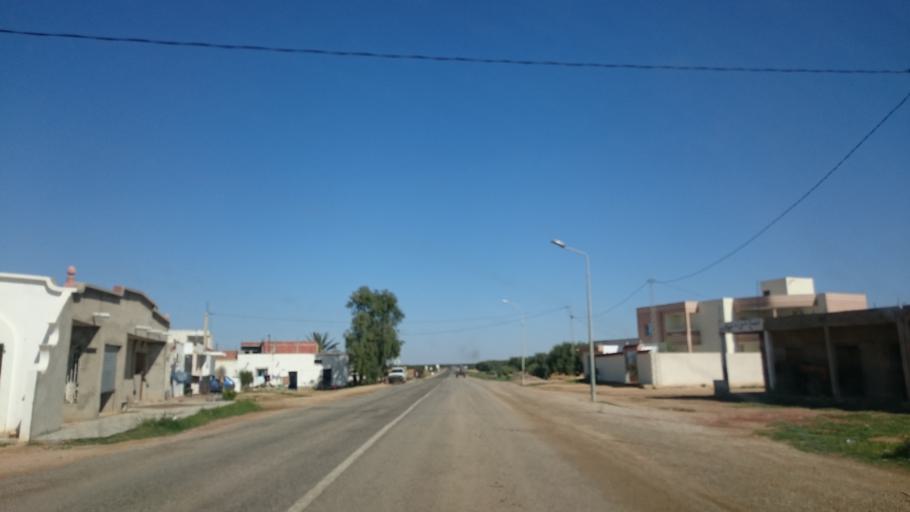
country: TN
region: Safaqis
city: Sfax
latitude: 34.8147
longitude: 10.4766
